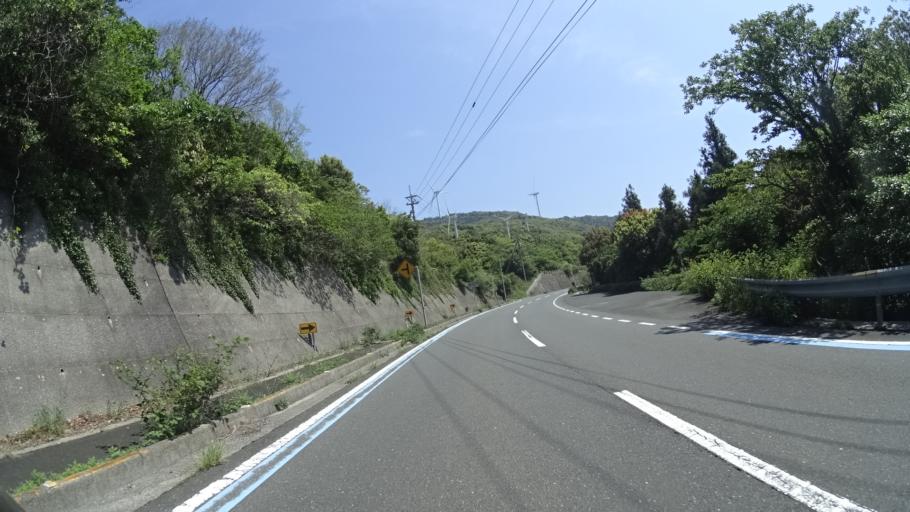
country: JP
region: Ehime
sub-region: Nishiuwa-gun
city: Ikata-cho
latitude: 33.4187
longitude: 132.1837
